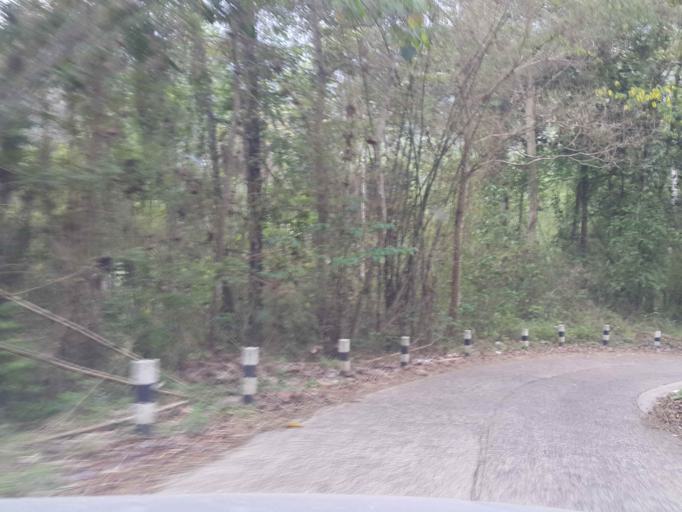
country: TH
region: Chiang Mai
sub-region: Amphoe Chiang Dao
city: Chiang Dao
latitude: 19.4150
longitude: 98.9122
